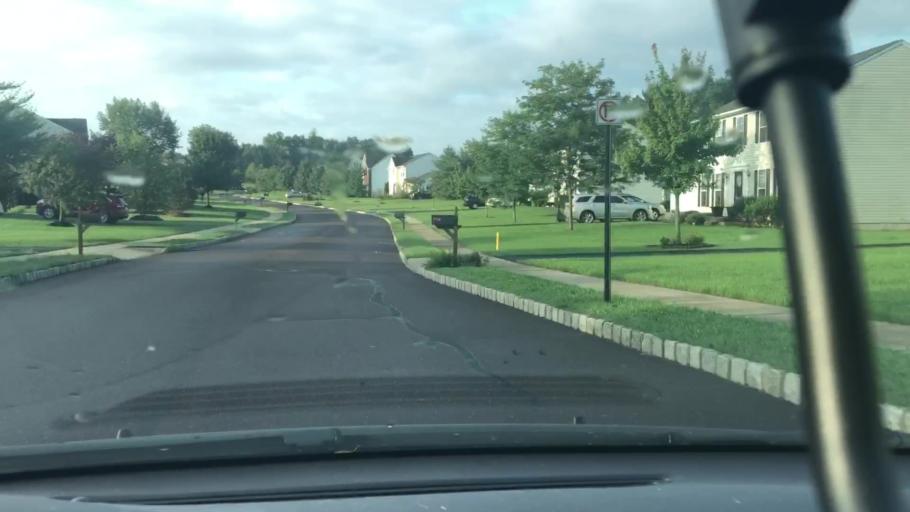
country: US
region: Pennsylvania
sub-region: Chester County
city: Kenilworth
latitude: 40.2168
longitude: -75.6187
